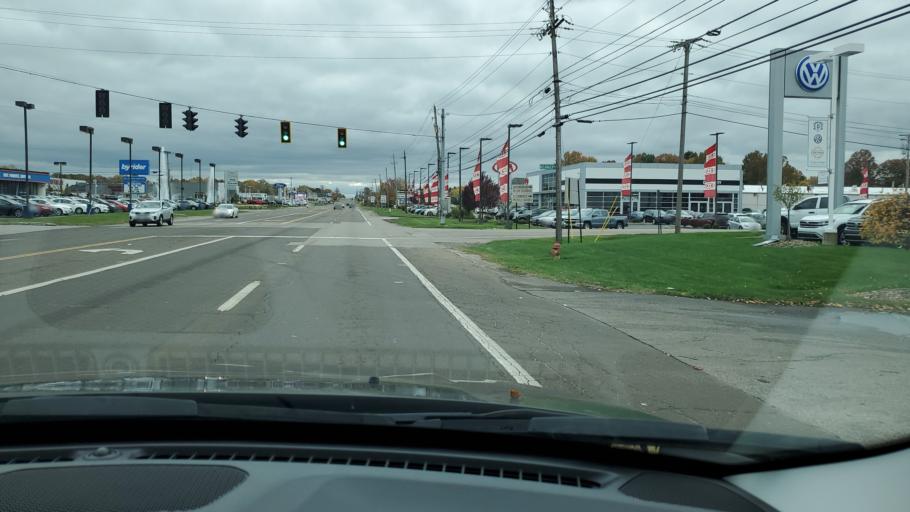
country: US
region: Ohio
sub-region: Mahoning County
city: Boardman
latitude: 41.0109
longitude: -80.6628
